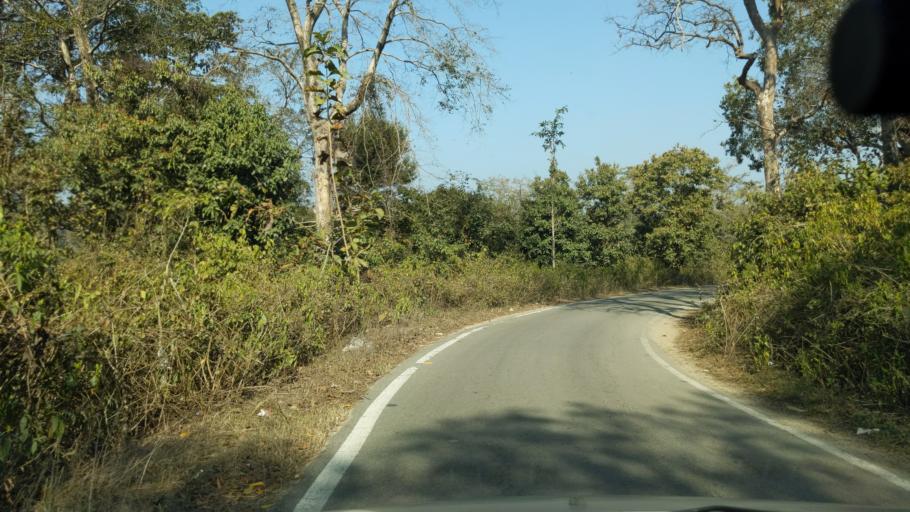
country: IN
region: Uttarakhand
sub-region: Naini Tal
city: Ramnagar
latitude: 29.4090
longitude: 79.1368
